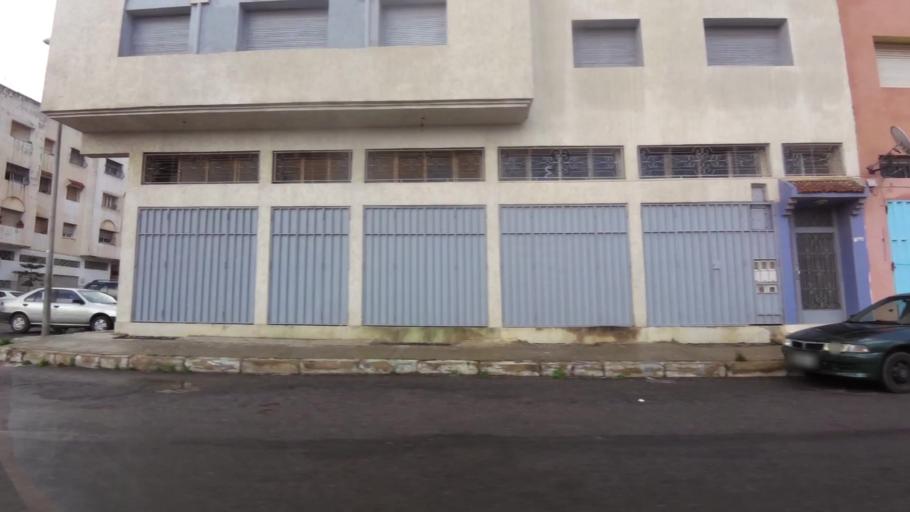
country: MA
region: Grand Casablanca
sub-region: Casablanca
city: Casablanca
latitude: 33.5389
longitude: -7.6860
